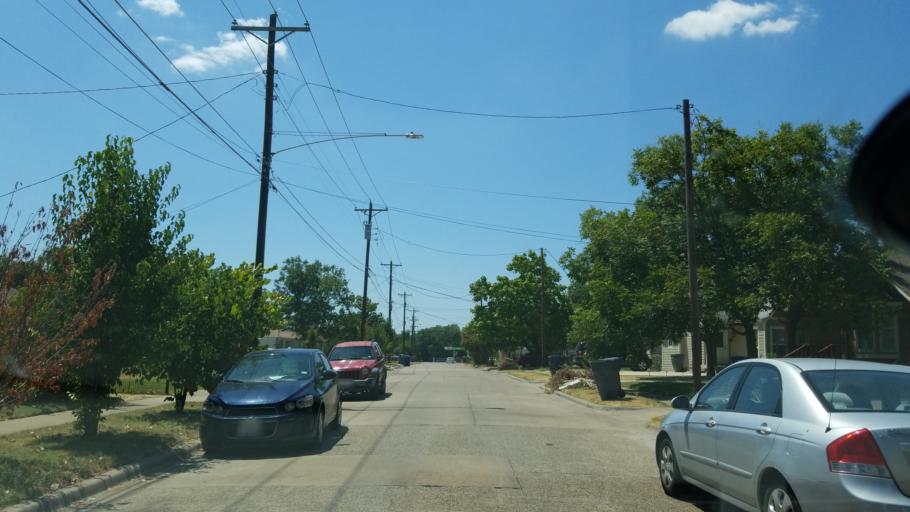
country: US
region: Texas
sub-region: Dallas County
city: Cockrell Hill
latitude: 32.7234
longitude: -96.8892
